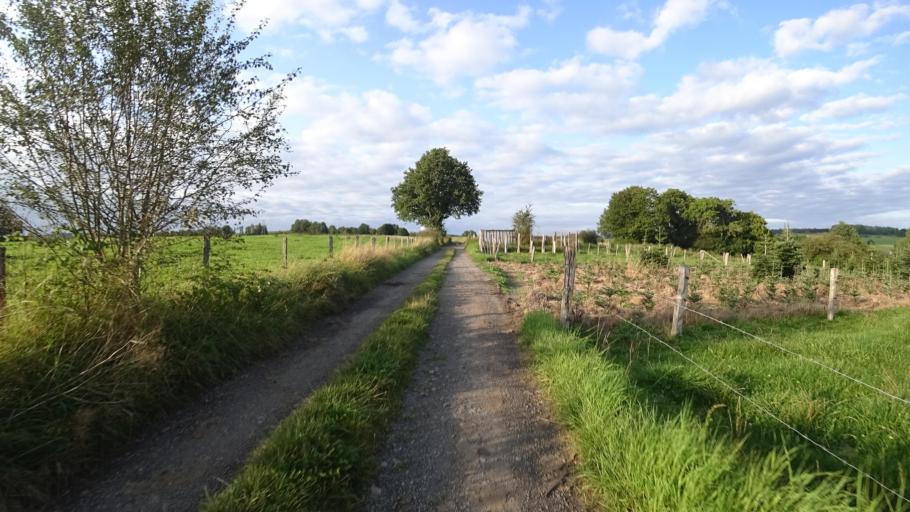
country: BE
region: Wallonia
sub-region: Province du Luxembourg
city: Neufchateau
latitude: 49.8592
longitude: 5.3692
